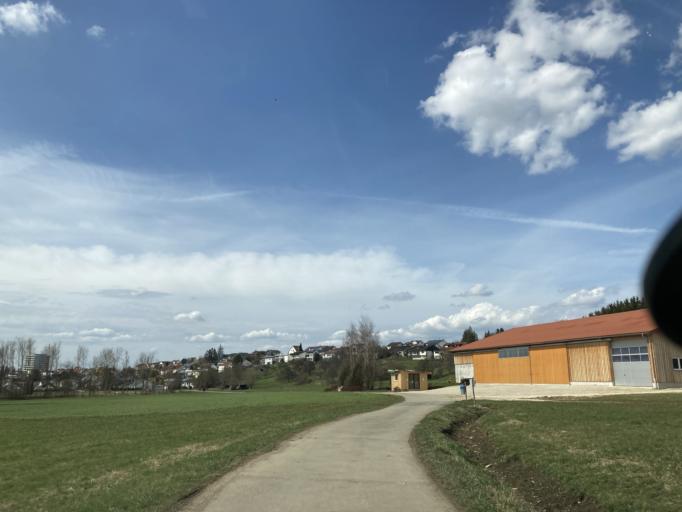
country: DE
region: Baden-Wuerttemberg
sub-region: Tuebingen Region
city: Gomaringen
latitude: 48.4568
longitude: 9.1138
